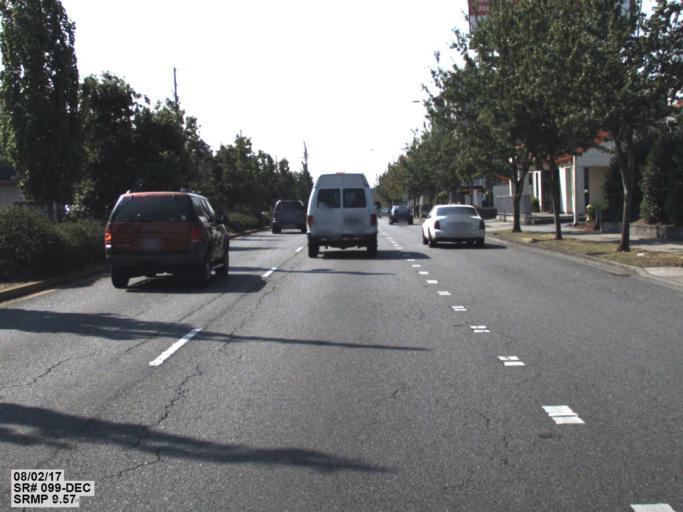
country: US
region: Washington
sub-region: King County
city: Federal Way
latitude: 47.3100
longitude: -122.3135
